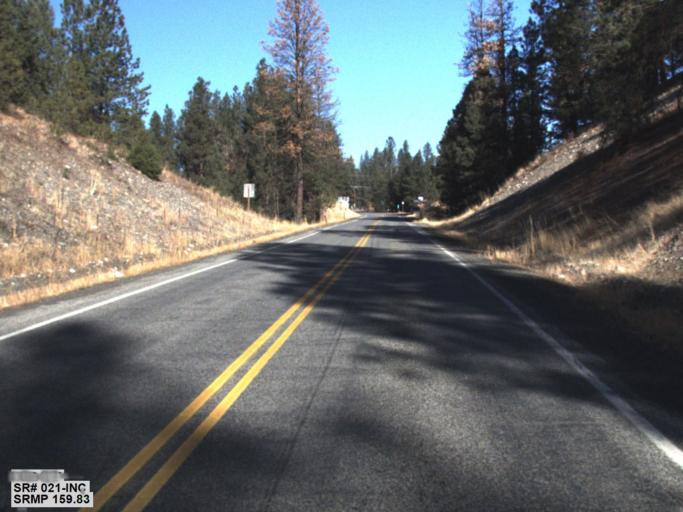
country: US
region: Washington
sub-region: Ferry County
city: Republic
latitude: 48.6369
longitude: -118.7315
